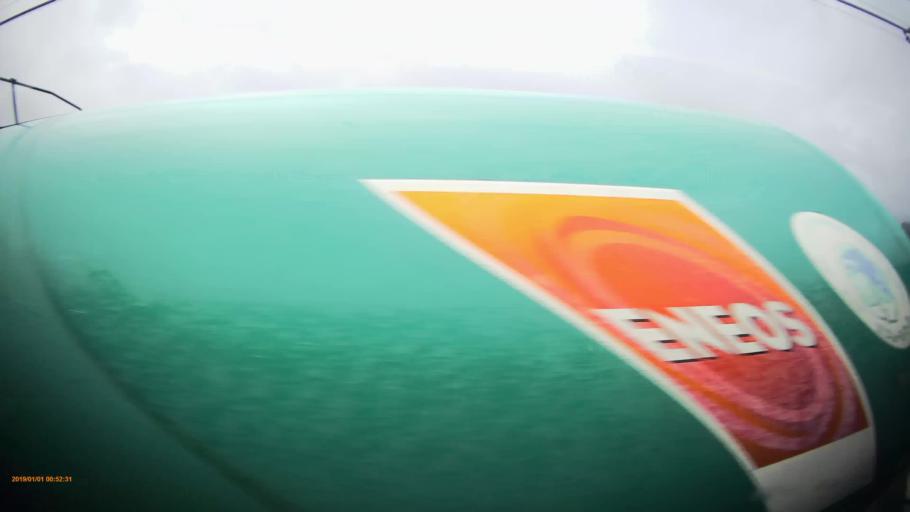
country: JP
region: Yamanashi
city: Otsuki
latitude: 35.5951
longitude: 138.8793
